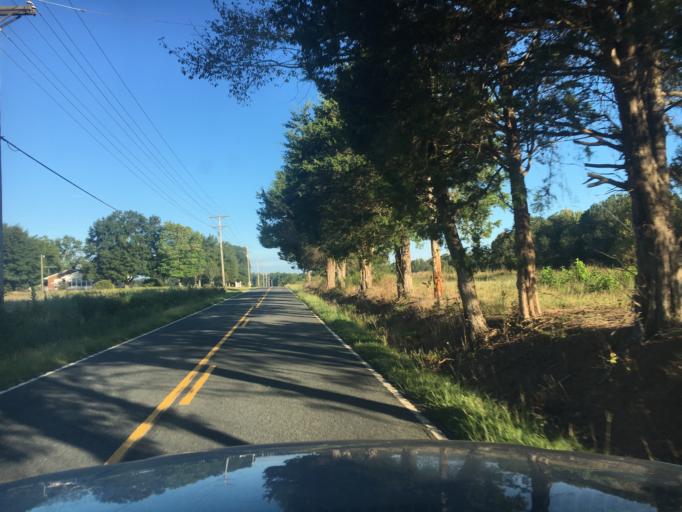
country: US
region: South Carolina
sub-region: Spartanburg County
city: Woodruff
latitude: 34.6325
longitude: -82.0433
